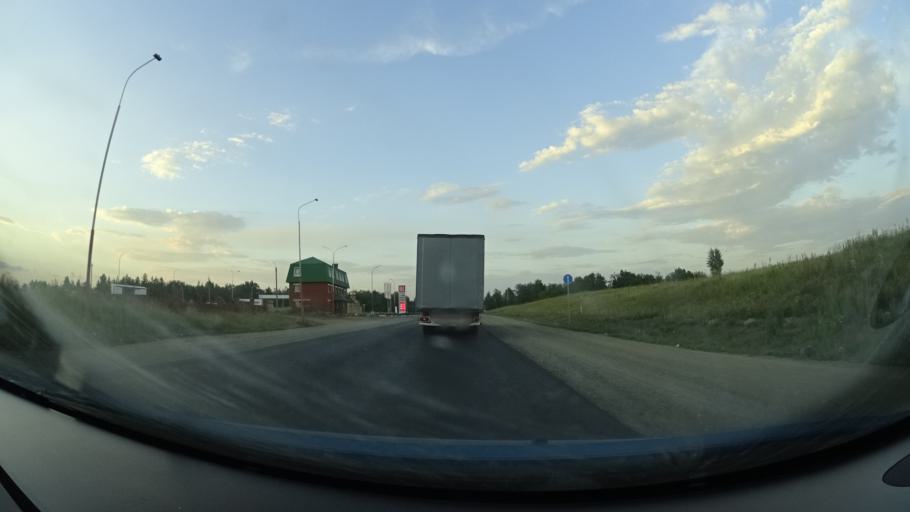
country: RU
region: Orenburg
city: Severnoye
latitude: 54.1504
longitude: 52.6165
